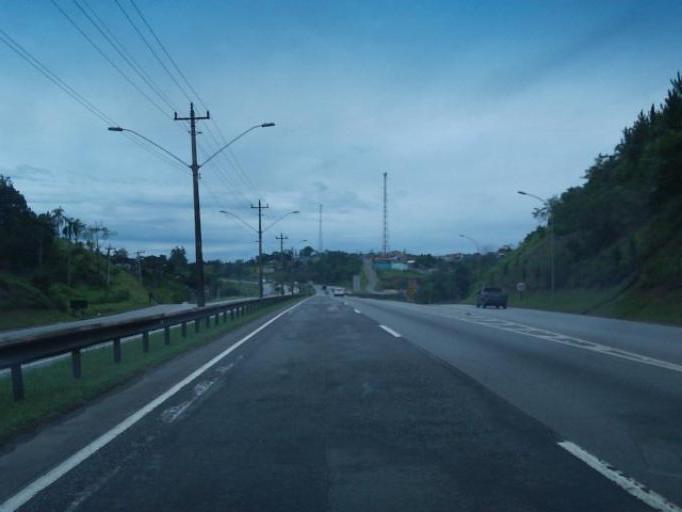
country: BR
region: Sao Paulo
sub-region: Sao Lourenco Da Serra
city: Sao Lourenco da Serra
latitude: -23.8570
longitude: -46.9422
